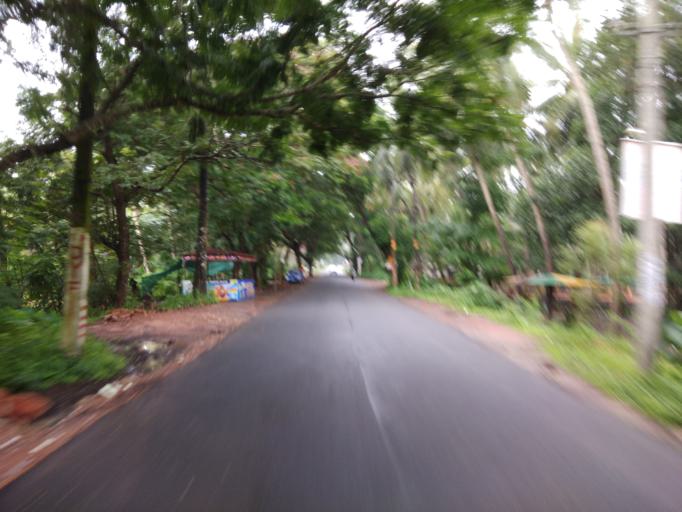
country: IN
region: Kerala
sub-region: Malappuram
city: Ponnani
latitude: 10.7597
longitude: 75.9738
